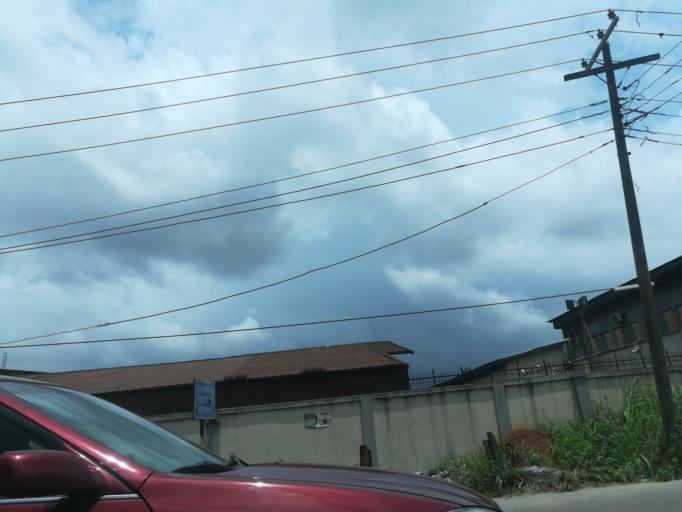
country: NG
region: Lagos
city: Oshodi
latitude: 6.5566
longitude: 3.3572
